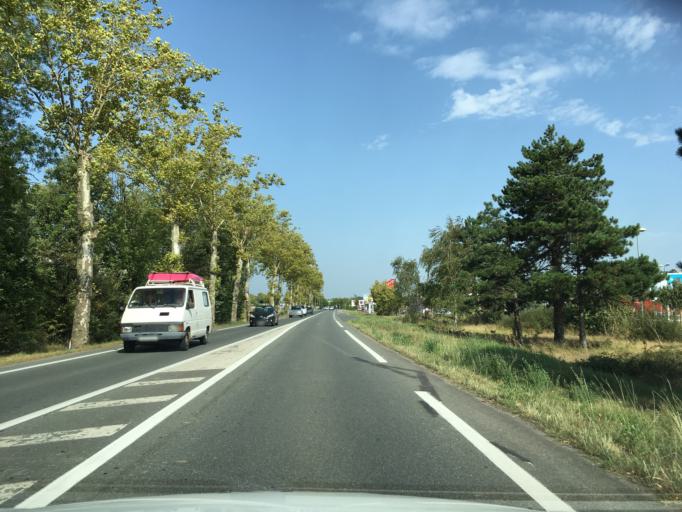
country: FR
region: Midi-Pyrenees
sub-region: Departement du Tarn
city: Lagarrigue
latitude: 43.5891
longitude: 2.2697
